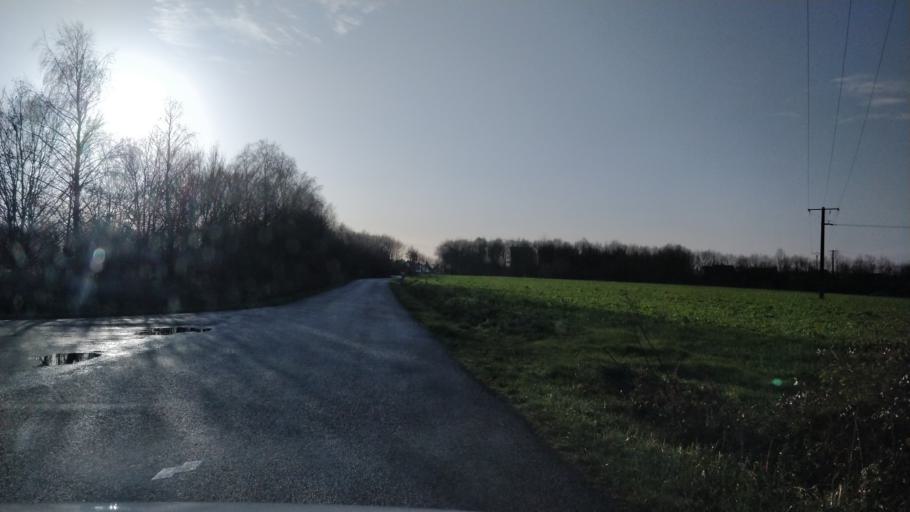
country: FR
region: Brittany
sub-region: Departement d'Ille-et-Vilaine
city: Chavagne
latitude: 48.0614
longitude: -1.7891
